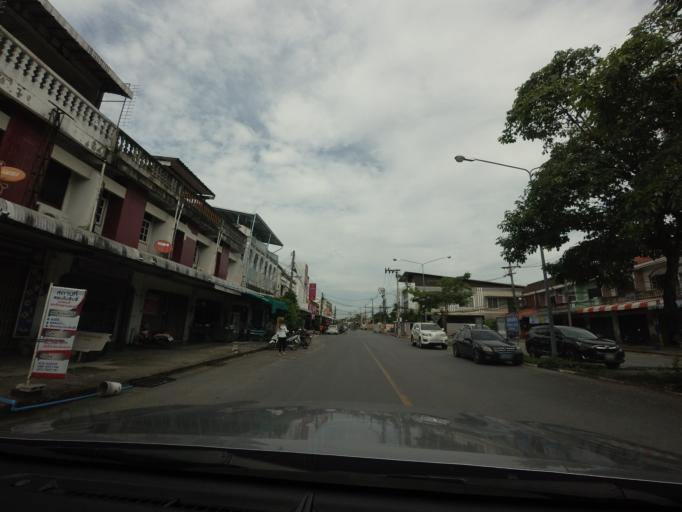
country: TH
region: Yala
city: Yala
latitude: 6.5439
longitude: 101.2908
